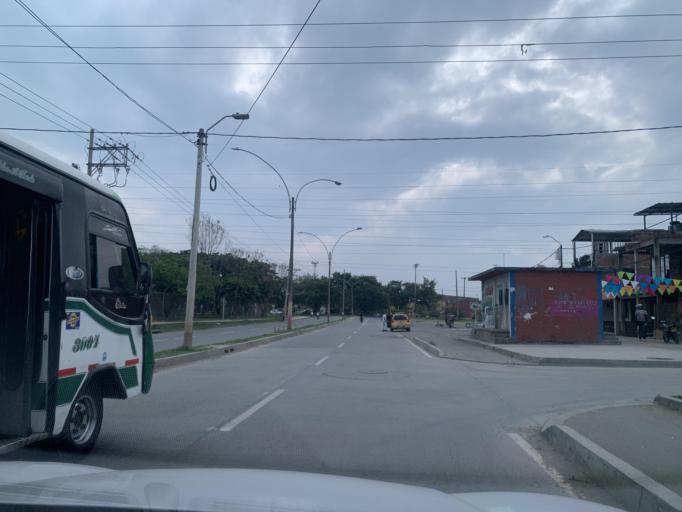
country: CO
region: Valle del Cauca
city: Cali
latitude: 3.4101
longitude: -76.4746
